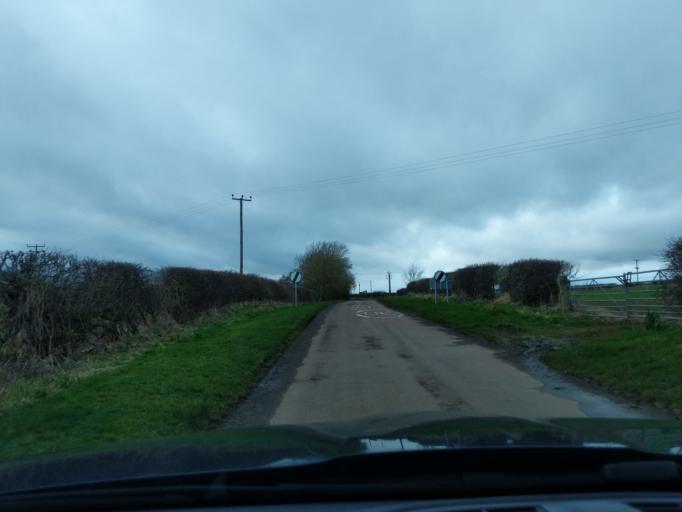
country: GB
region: England
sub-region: Northumberland
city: Ancroft
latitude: 55.7004
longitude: -2.0072
